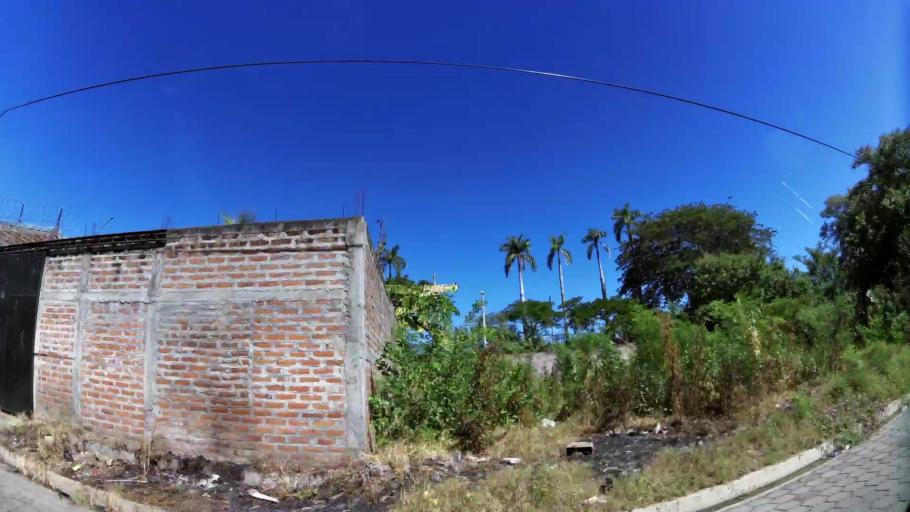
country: SV
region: San Miguel
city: San Miguel
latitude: 13.4813
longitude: -88.1693
